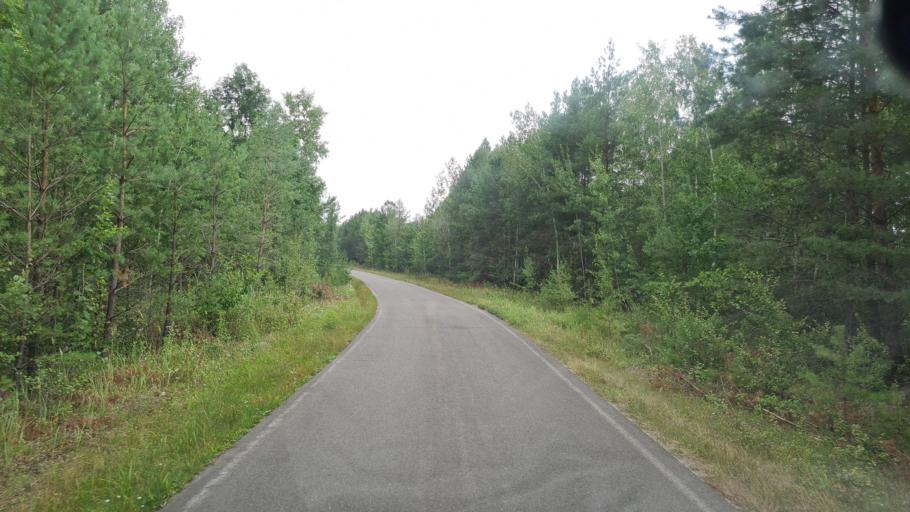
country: DE
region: Brandenburg
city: Finsterwalde
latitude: 51.5776
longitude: 13.7564
